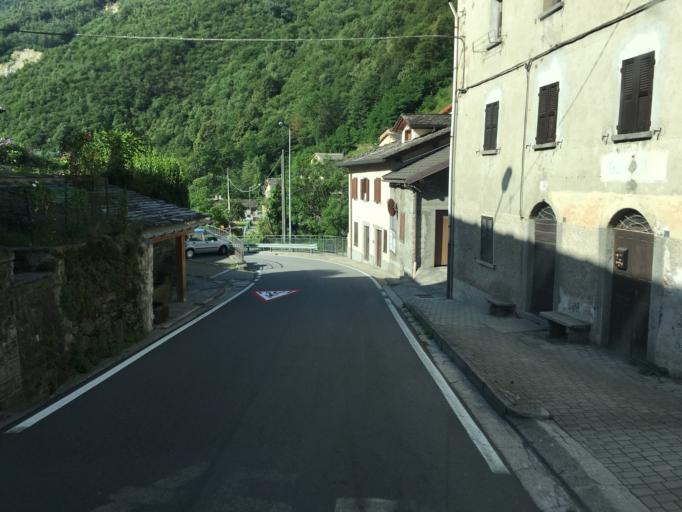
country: IT
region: Lombardy
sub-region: Provincia di Sondrio
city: San Giacomo Filippo
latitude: 46.3368
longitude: 9.3698
